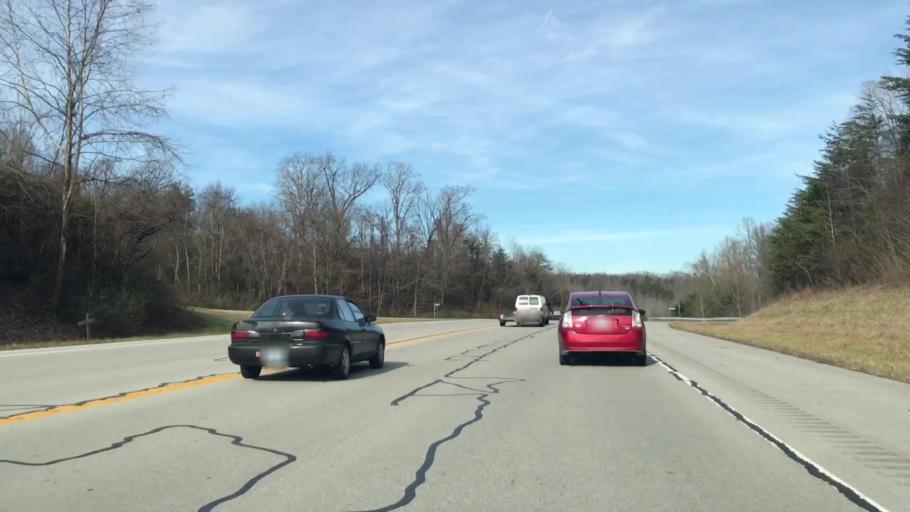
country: US
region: Kentucky
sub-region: McCreary County
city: Whitley City
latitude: 36.8092
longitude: -84.4879
